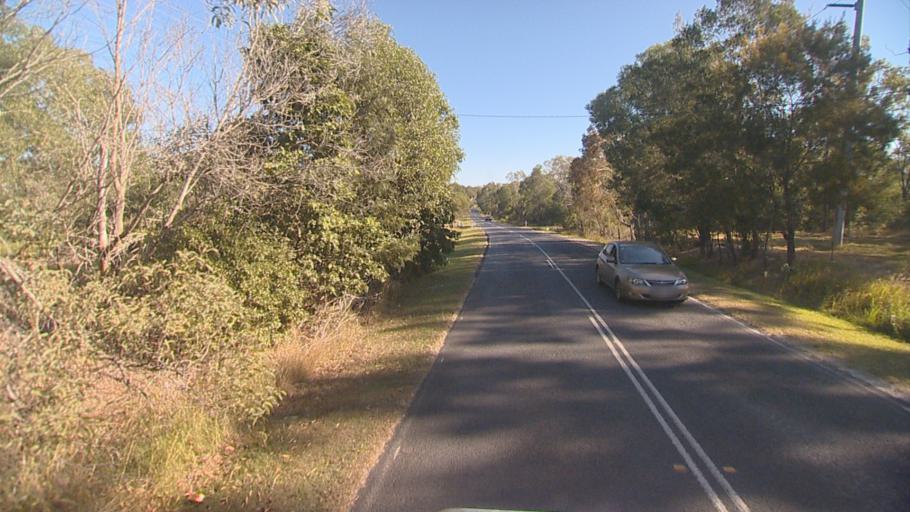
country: AU
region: Queensland
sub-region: Logan
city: North Maclean
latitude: -27.7833
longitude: 153.0528
